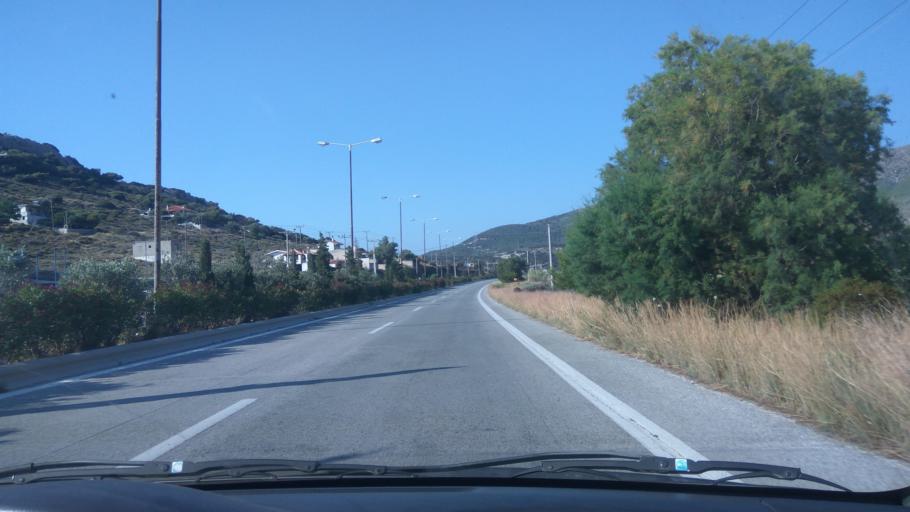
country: GR
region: Attica
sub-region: Nomarchia Anatolikis Attikis
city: Lavrio
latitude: 37.7788
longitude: 24.0566
